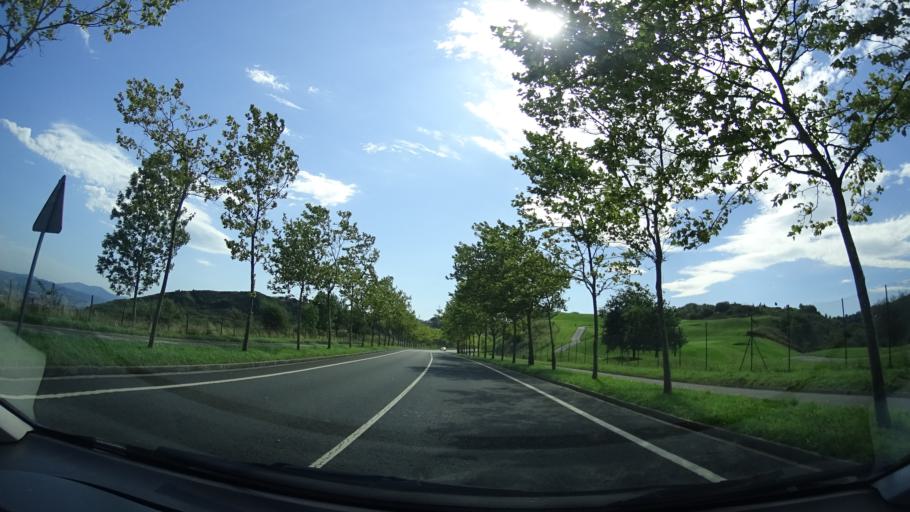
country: ES
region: Basque Country
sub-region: Bizkaia
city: Urtuella
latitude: 43.2929
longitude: -3.0629
